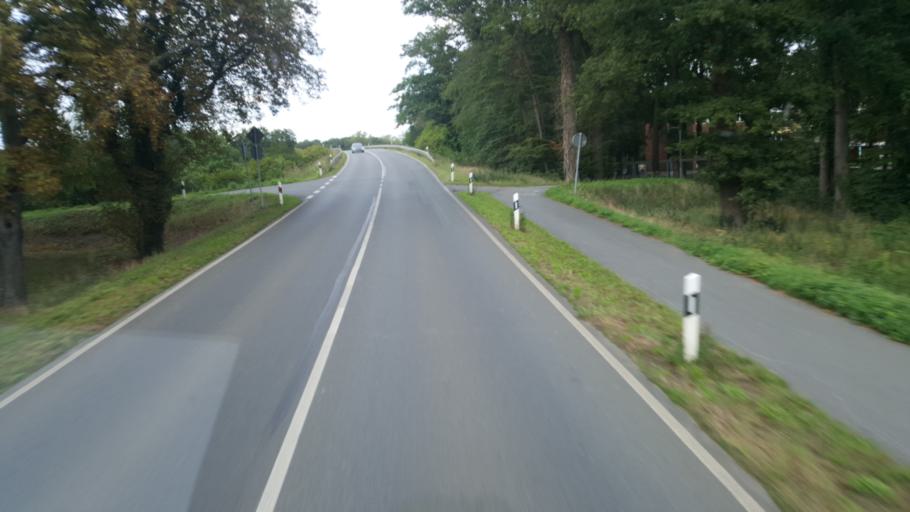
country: DE
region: North Rhine-Westphalia
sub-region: Regierungsbezirk Dusseldorf
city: Voerde
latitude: 51.5860
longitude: 6.7013
